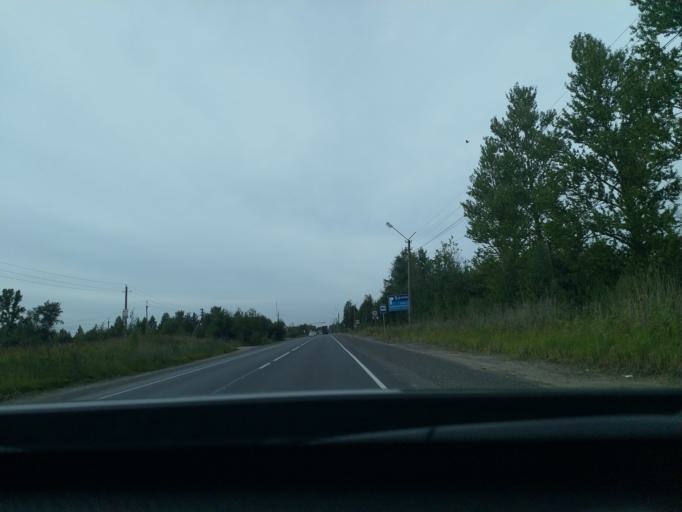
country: RU
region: Leningrad
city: Nikol'skoye
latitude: 59.7214
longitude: 30.7785
